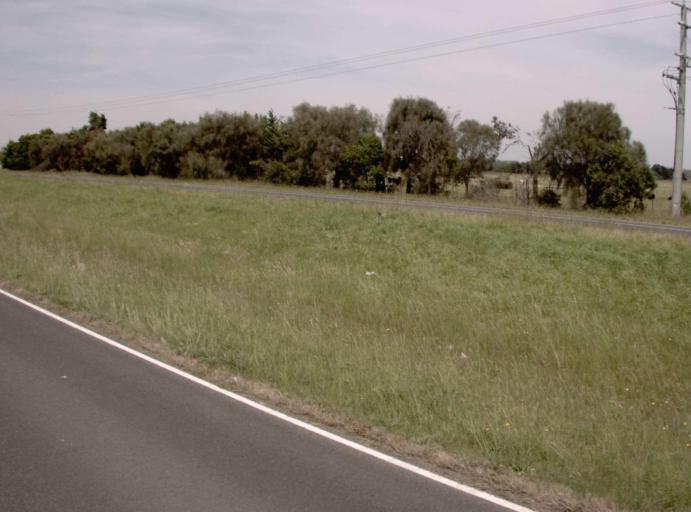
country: AU
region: Victoria
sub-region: Frankston
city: Skye
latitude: -38.0889
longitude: 145.2374
